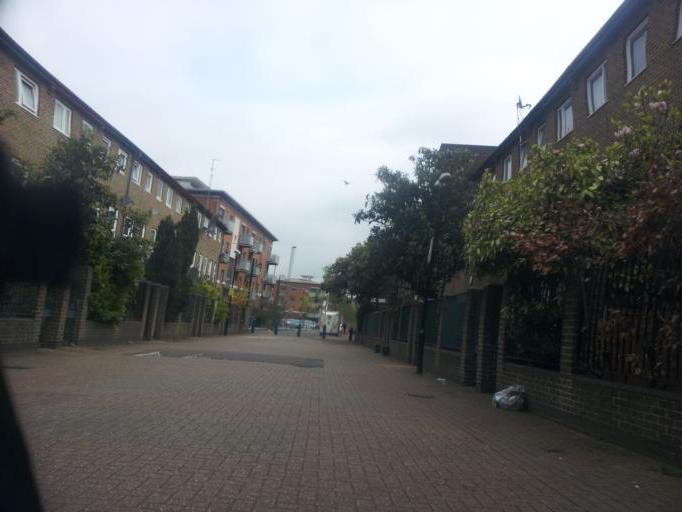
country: GB
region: England
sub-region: Greater London
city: Lambeth
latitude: 51.4917
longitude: -0.1175
